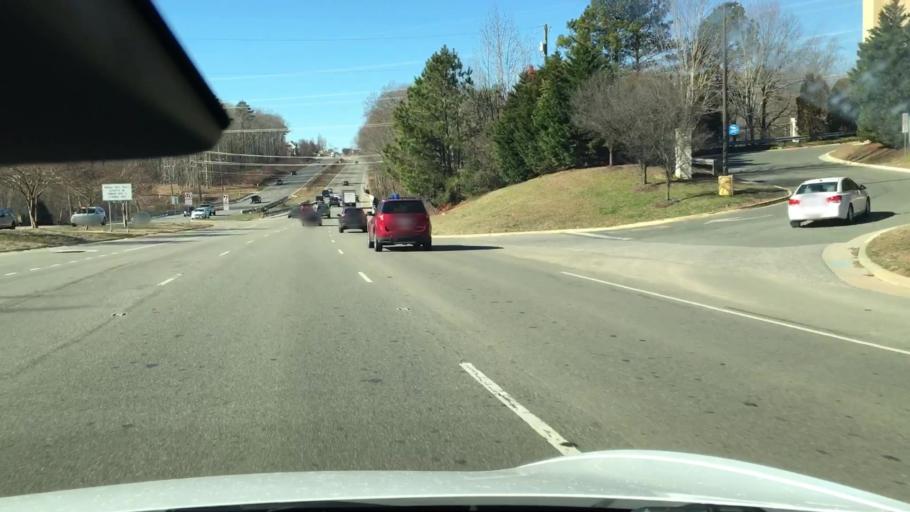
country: US
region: Virginia
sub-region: Chesterfield County
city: Brandermill
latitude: 37.5032
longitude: -77.6302
